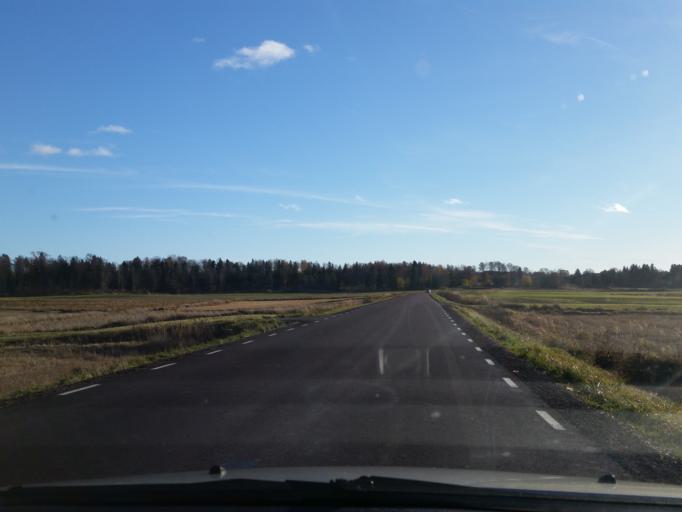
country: AX
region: Alands landsbygd
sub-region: Jomala
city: Jomala
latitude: 60.1959
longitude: 19.9586
